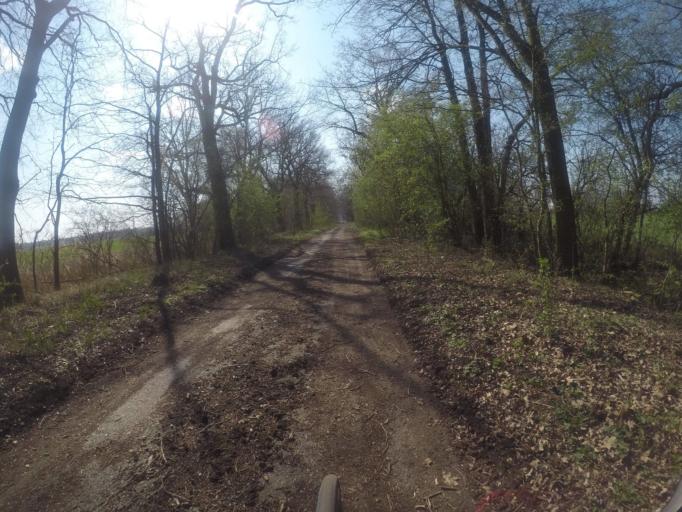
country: DE
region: Brandenburg
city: Nauen
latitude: 52.6552
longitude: 12.9189
